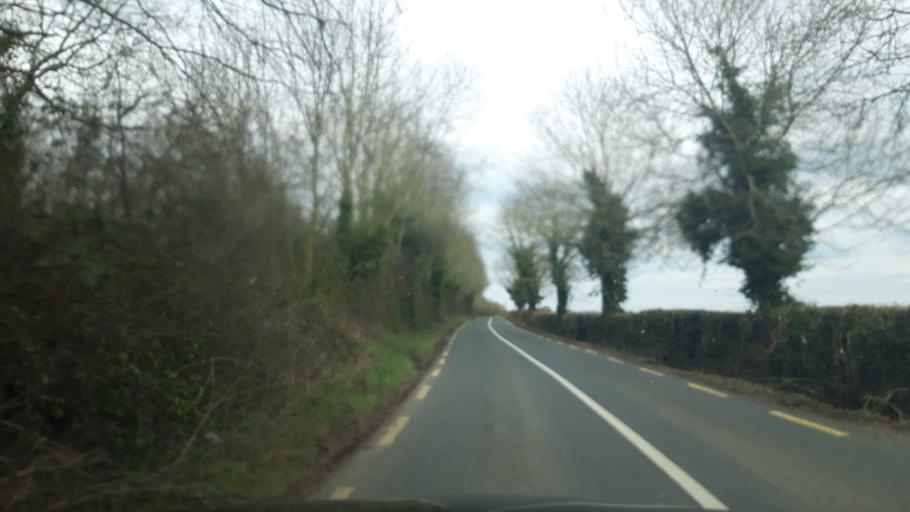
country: IE
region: Leinster
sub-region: Kildare
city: Rathangan
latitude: 53.2498
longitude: -6.9481
